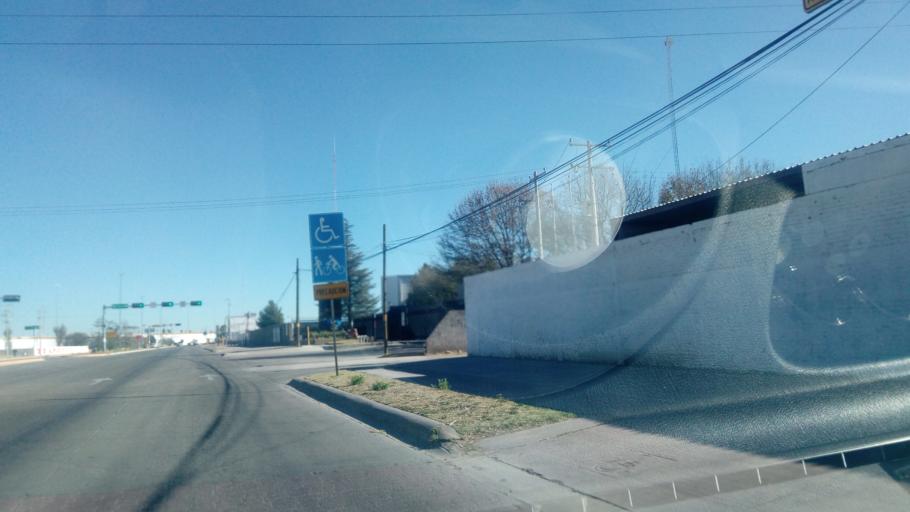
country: MX
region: Durango
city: Victoria de Durango
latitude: 24.0903
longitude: -104.5793
